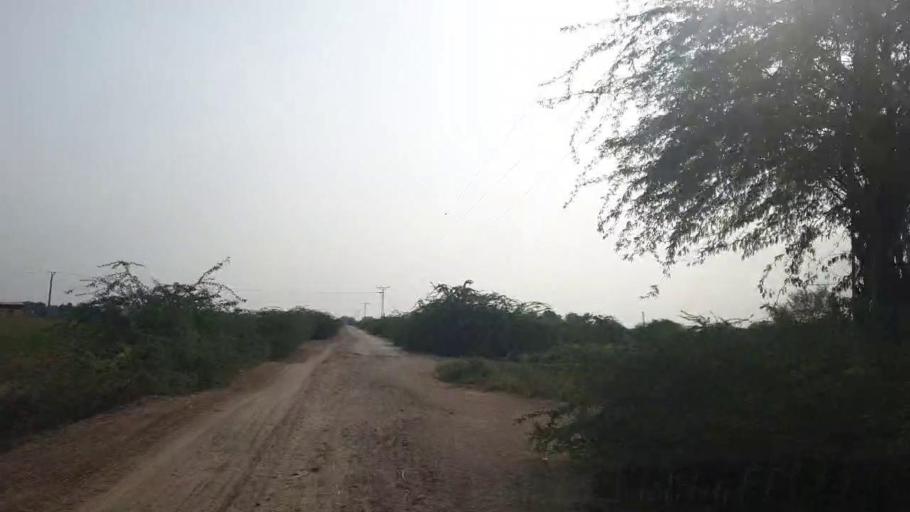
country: PK
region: Sindh
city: Badin
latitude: 24.6192
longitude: 68.6876
